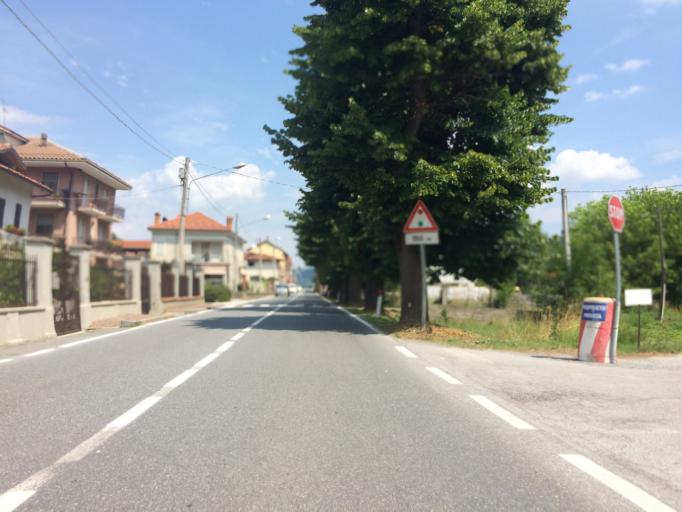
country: IT
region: Piedmont
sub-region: Provincia di Cuneo
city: Bagnasco
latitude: 44.3059
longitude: 8.0458
